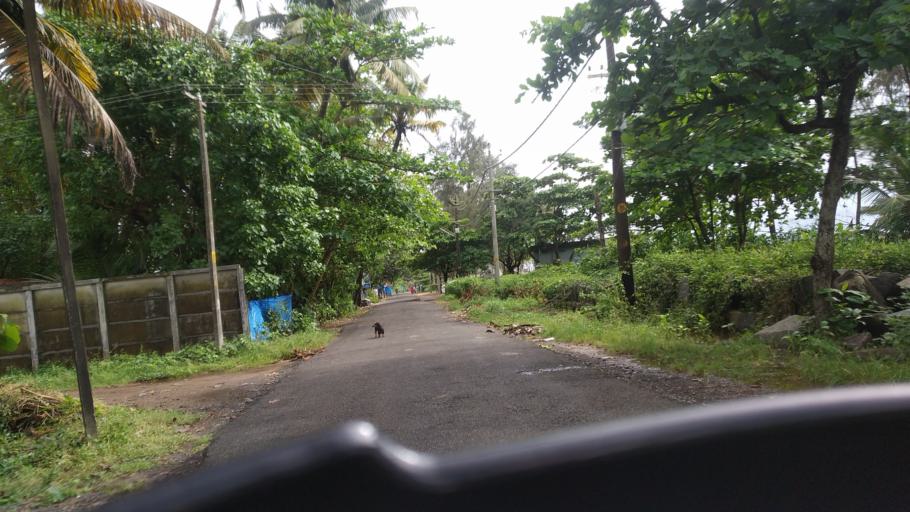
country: IN
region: Kerala
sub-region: Thrissur District
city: Kodungallur
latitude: 10.1286
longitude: 76.1827
